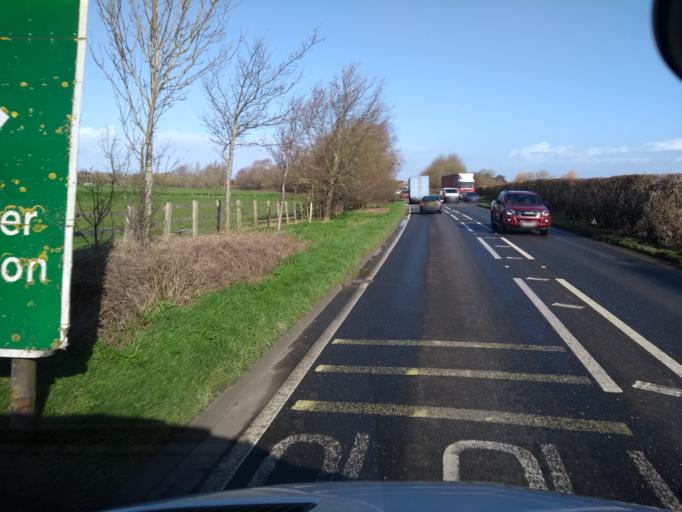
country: GB
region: England
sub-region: Somerset
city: Ilchester
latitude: 50.9962
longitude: -2.6805
